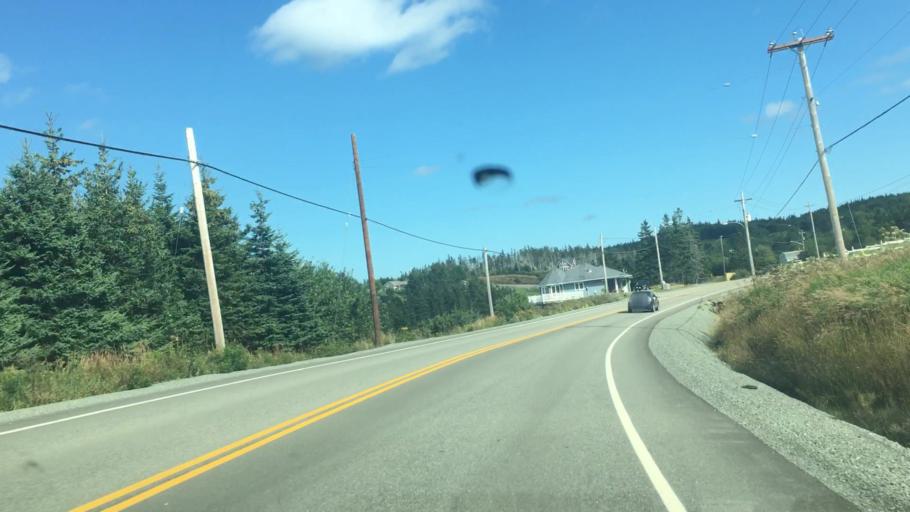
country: CA
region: Nova Scotia
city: Princeville
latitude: 45.6505
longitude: -60.8490
